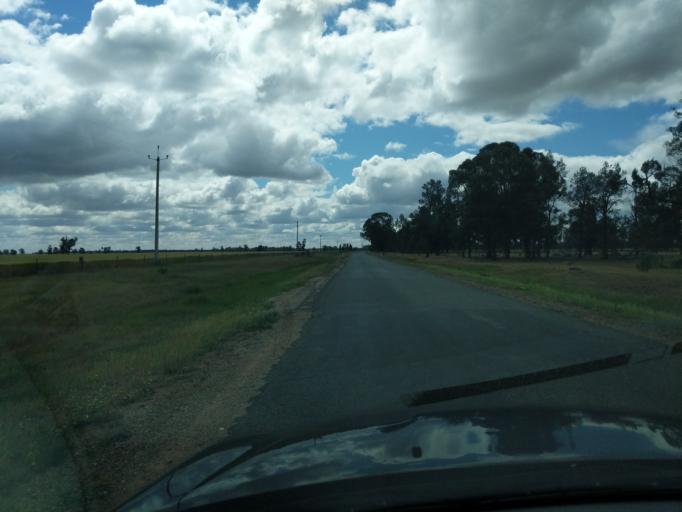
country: AU
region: New South Wales
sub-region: Coolamon
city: Coolamon
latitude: -34.8654
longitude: 146.8969
